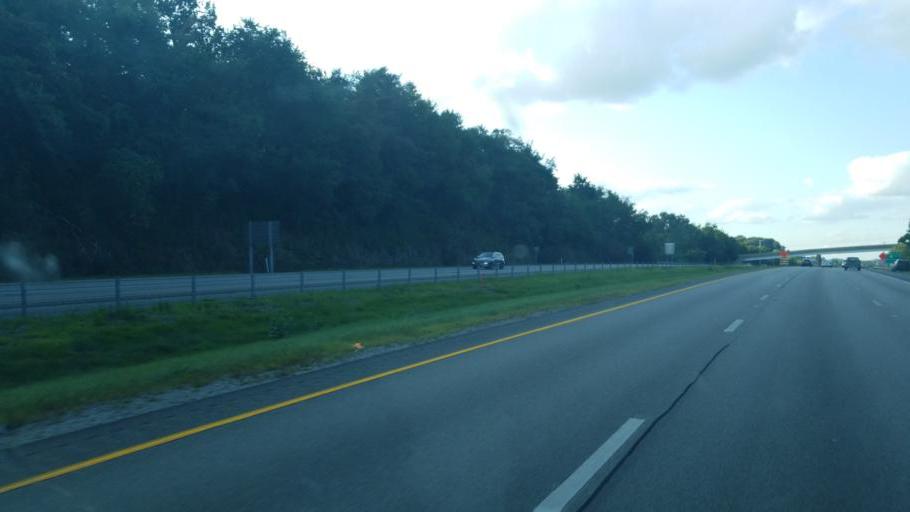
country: US
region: Pennsylvania
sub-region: Allegheny County
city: Bradford Woods
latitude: 40.6384
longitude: -80.0977
